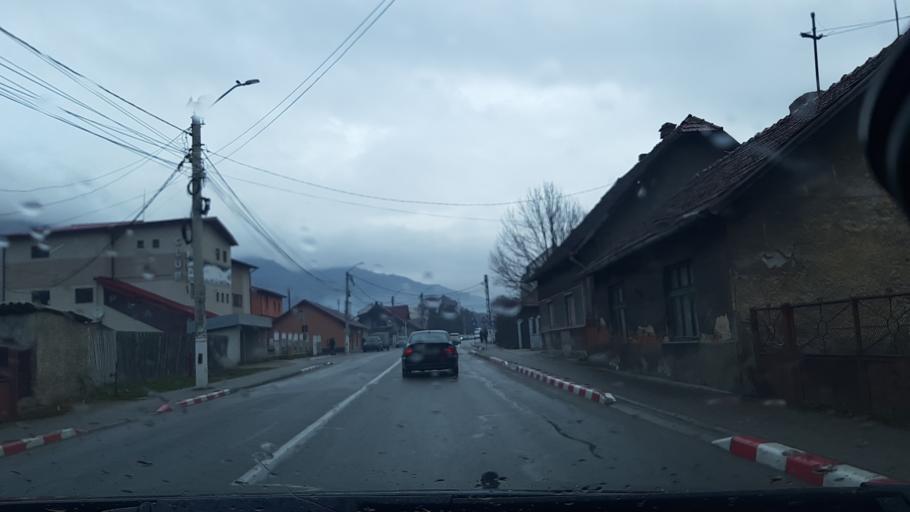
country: RO
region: Hunedoara
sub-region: Municipiul Petrosani
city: Petrosani
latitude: 45.4412
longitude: 23.3714
